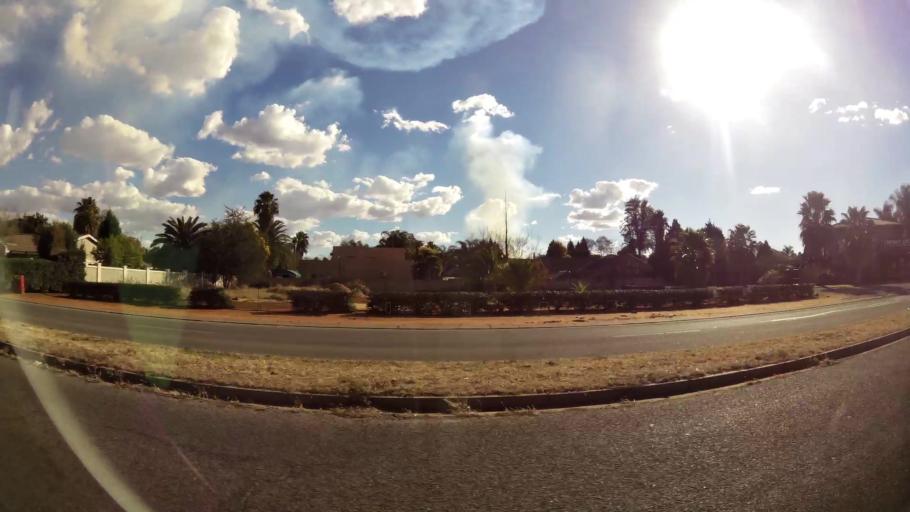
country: ZA
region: North-West
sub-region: Dr Kenneth Kaunda District Municipality
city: Klerksdorp
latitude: -26.8337
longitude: 26.6789
